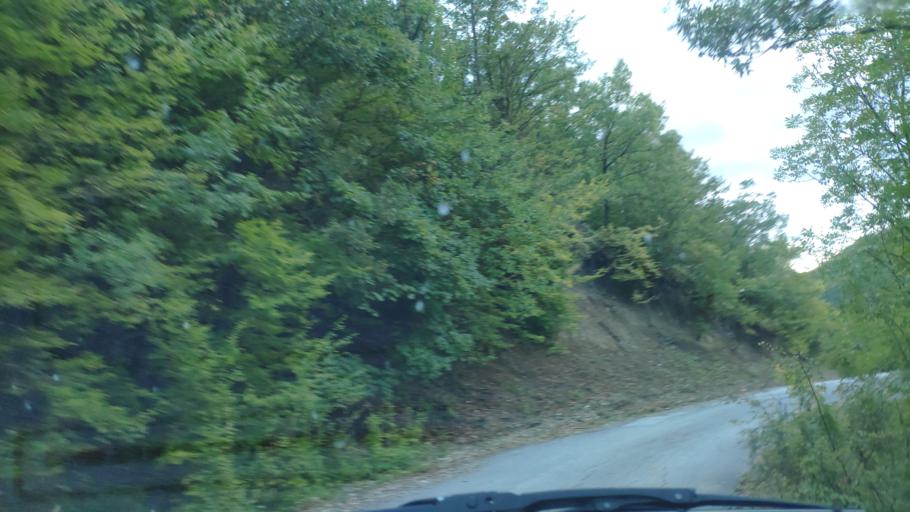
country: AL
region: Korce
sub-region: Rrethi i Kolonjes
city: Erseke
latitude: 40.2500
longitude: 20.8666
